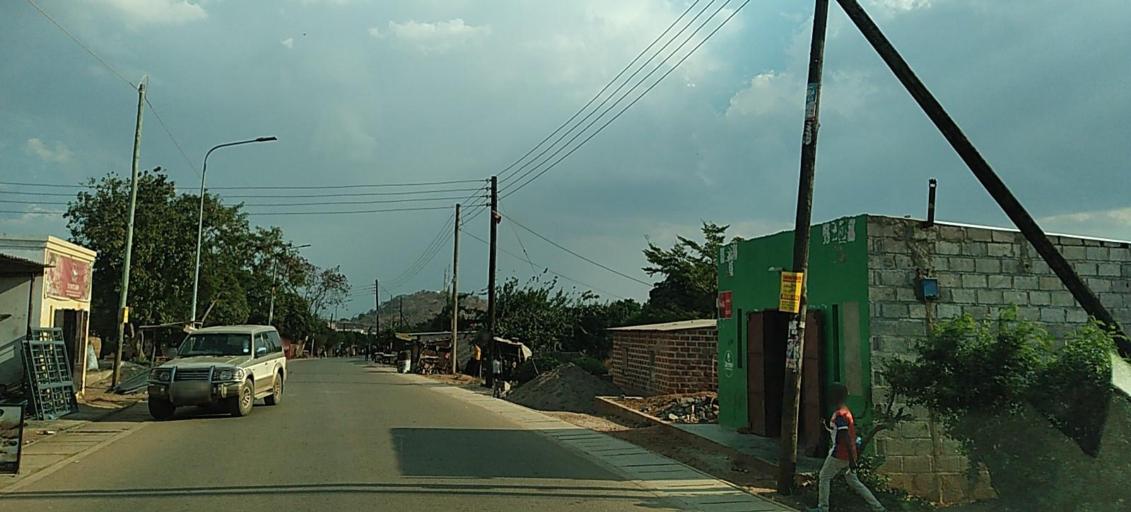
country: ZM
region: Lusaka
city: Lusaka
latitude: -15.5323
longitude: 28.2368
